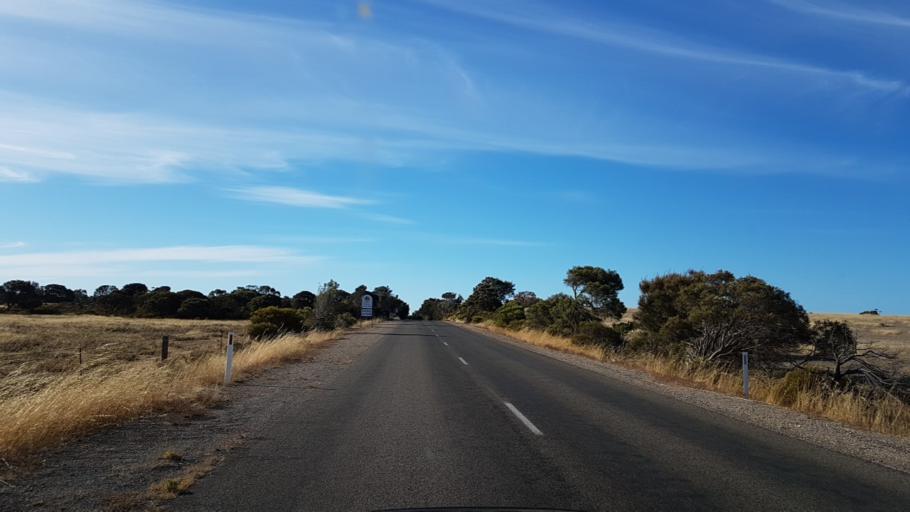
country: AU
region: South Australia
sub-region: Yorke Peninsula
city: Port Victoria
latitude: -34.9300
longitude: 137.0863
